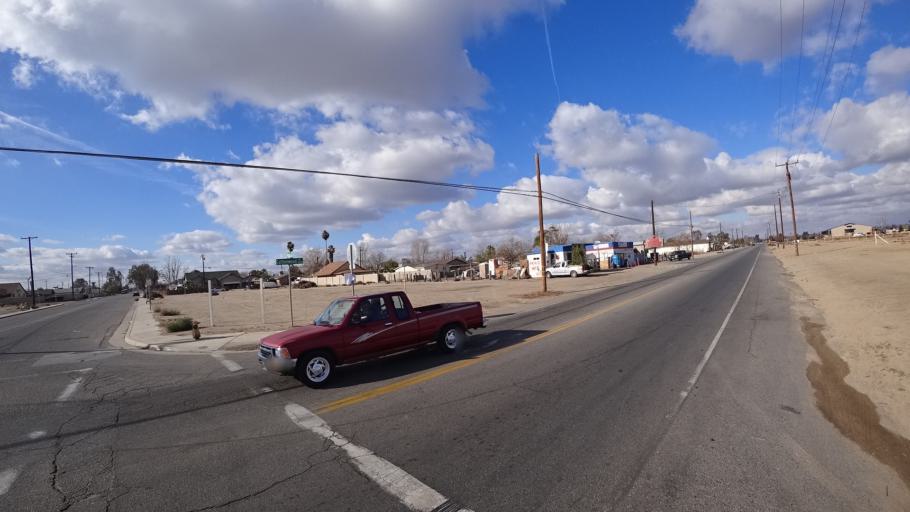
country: US
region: California
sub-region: Kern County
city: Bakersfield
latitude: 35.3250
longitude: -118.9854
